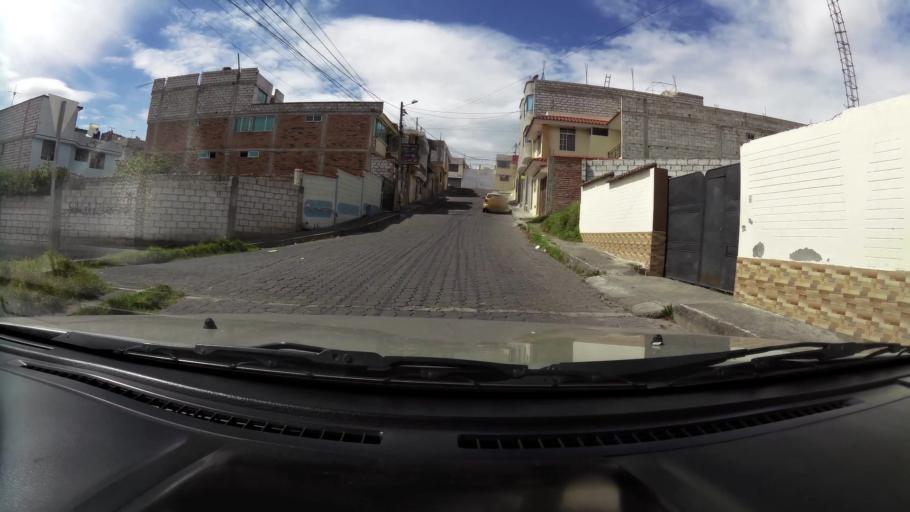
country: EC
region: Cotopaxi
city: Latacunga
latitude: -0.9311
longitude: -78.6042
